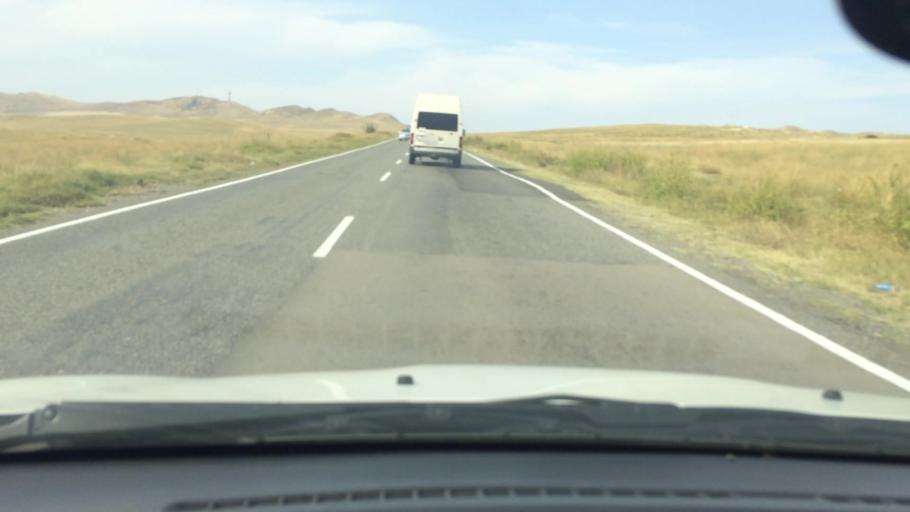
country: GE
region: Kvemo Kartli
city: Rust'avi
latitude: 41.5260
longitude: 44.9815
